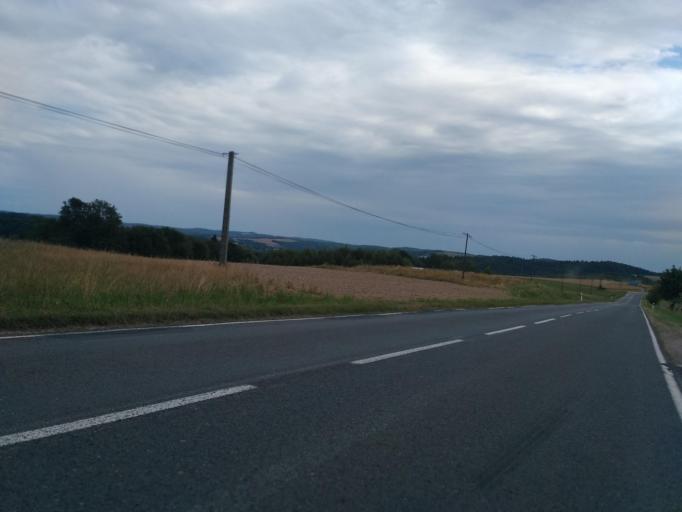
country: PL
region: Subcarpathian Voivodeship
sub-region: Powiat przeworski
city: Jawornik Polski
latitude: 49.8914
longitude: 22.2354
